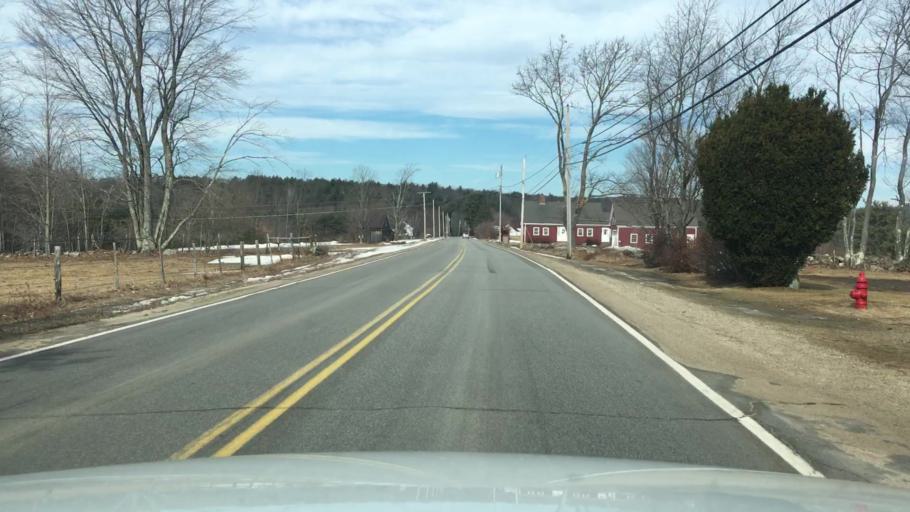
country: US
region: Maine
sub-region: York County
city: Springvale
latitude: 43.4948
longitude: -70.8102
